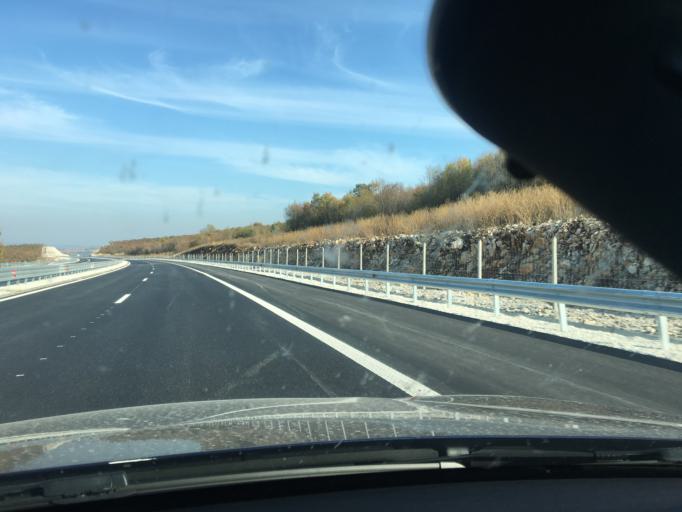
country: BG
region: Lovech
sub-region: Obshtina Yablanitsa
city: Yablanitsa
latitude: 43.0496
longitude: 24.1526
